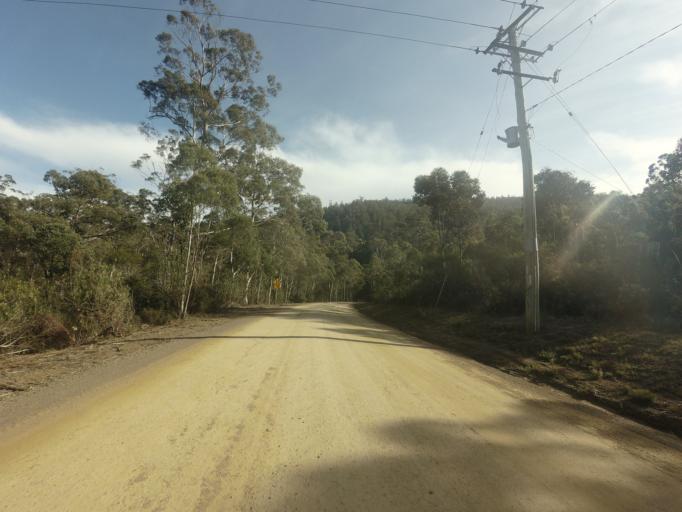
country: AU
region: Tasmania
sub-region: Huon Valley
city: Huonville
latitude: -43.0633
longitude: 147.0916
